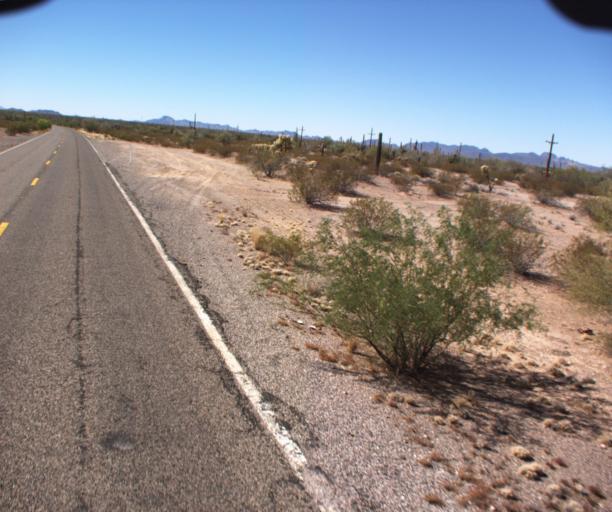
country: US
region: Arizona
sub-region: Pima County
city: Ajo
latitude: 32.2240
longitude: -112.7560
